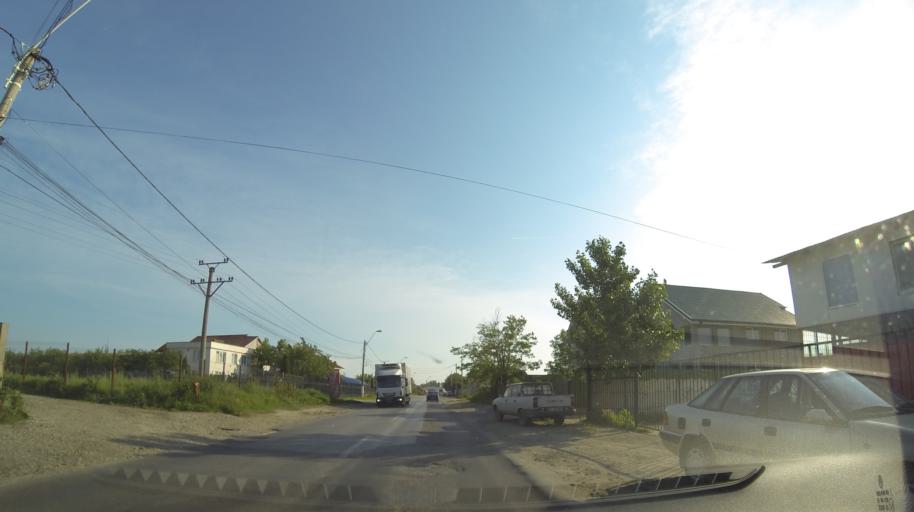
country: RO
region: Olt
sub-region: Municipiul Slatina
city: Slatina
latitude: 44.4366
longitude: 24.3647
